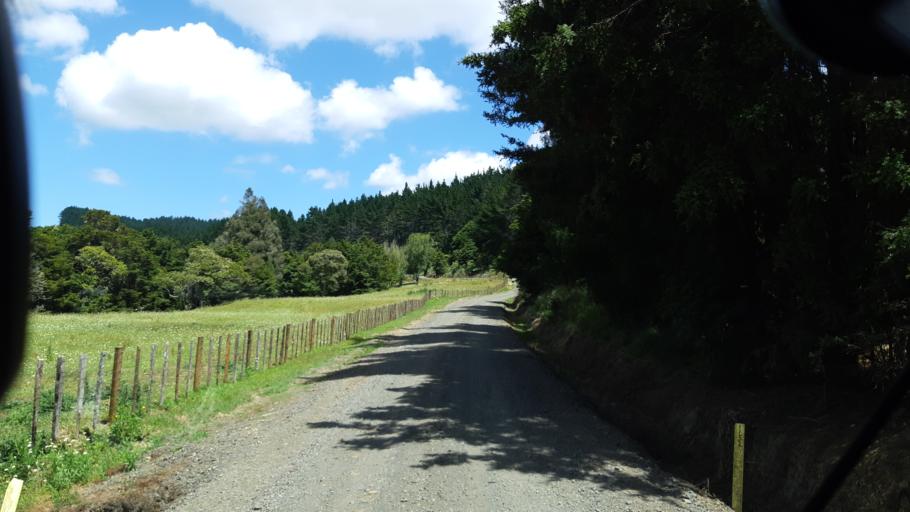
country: NZ
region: Northland
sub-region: Far North District
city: Kaitaia
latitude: -35.2413
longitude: 173.3078
